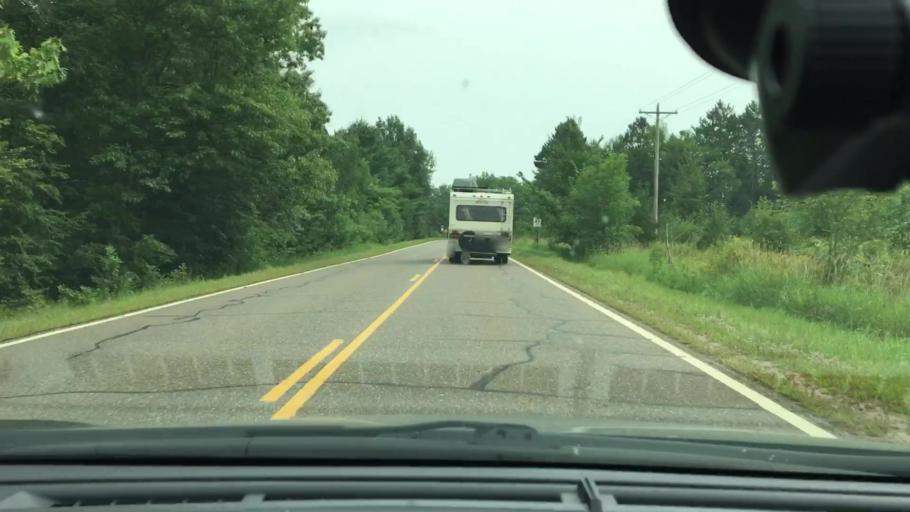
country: US
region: Minnesota
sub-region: Aitkin County
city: Aitkin
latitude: 46.4021
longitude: -93.7641
